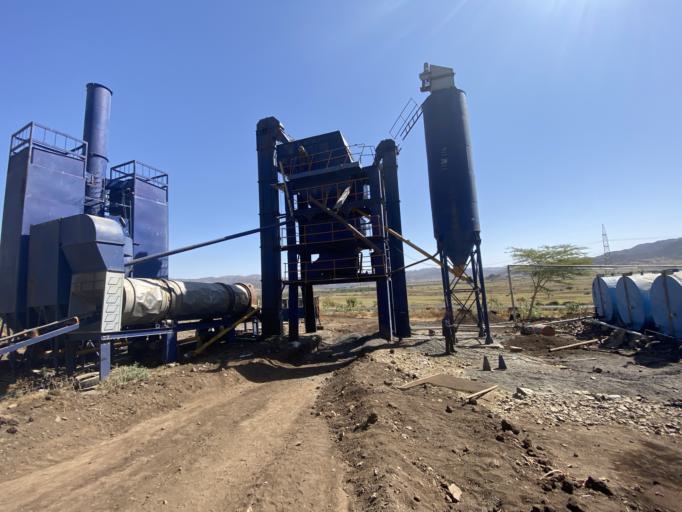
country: ET
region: Amhara
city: Robit
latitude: 11.8873
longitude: 39.6852
